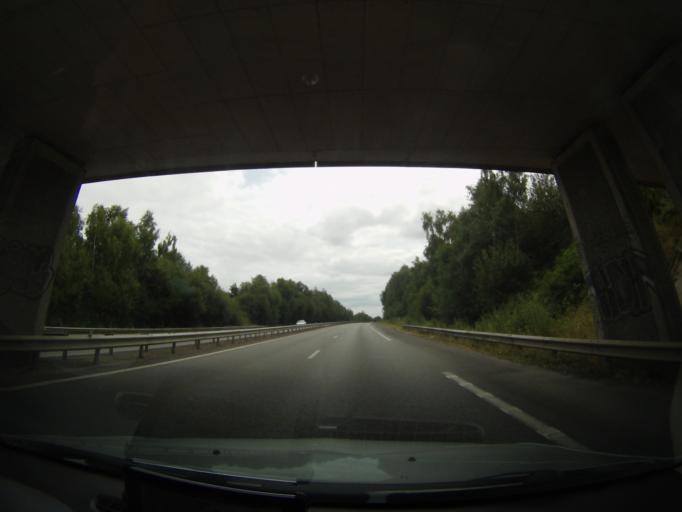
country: FR
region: Pays de la Loire
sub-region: Departement de la Loire-Atlantique
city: Orvault
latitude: 47.2897
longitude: -1.6094
